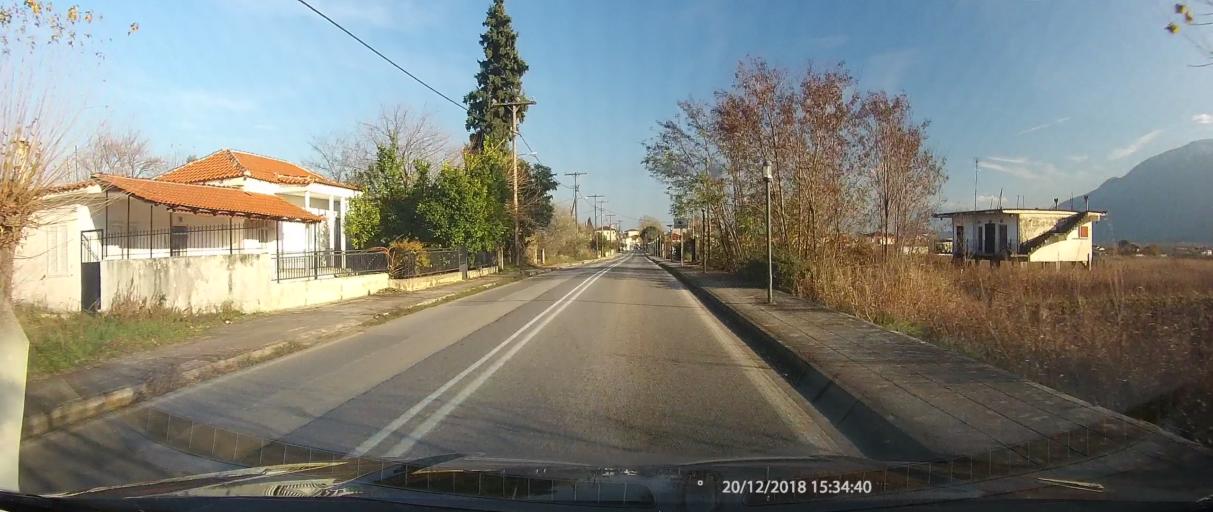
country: GR
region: Central Greece
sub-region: Nomos Fthiotidos
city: Lianokladhion
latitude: 38.9181
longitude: 22.2972
